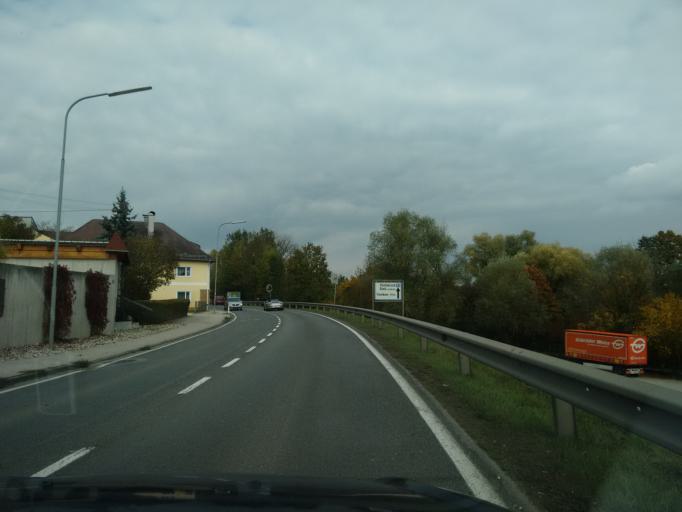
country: AT
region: Upper Austria
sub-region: Politischer Bezirk Vocklabruck
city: Timelkam
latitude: 47.9890
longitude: 13.6160
